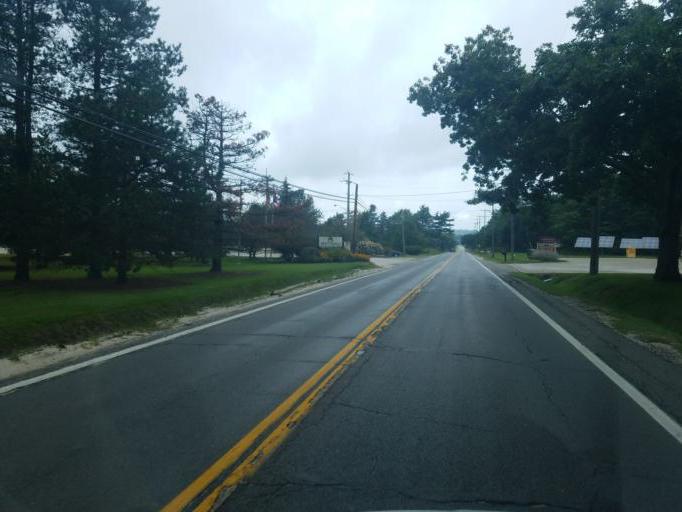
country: US
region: Ohio
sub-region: Geauga County
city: Chardon
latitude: 41.5494
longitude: -81.1959
